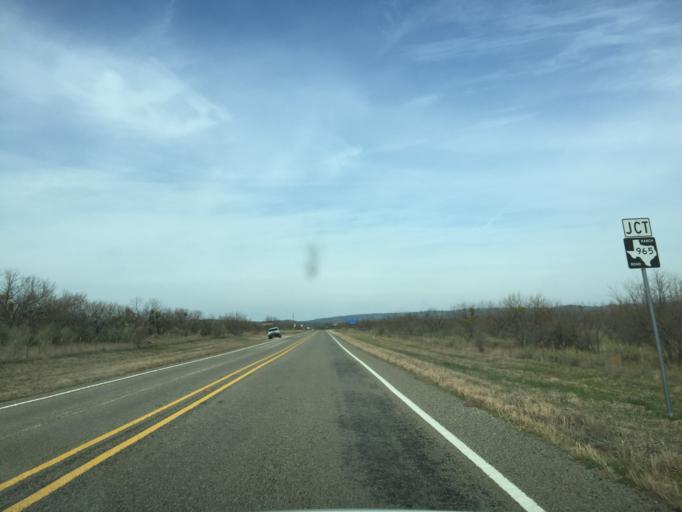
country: US
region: Texas
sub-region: Llano County
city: Llano
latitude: 30.5404
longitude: -98.7055
